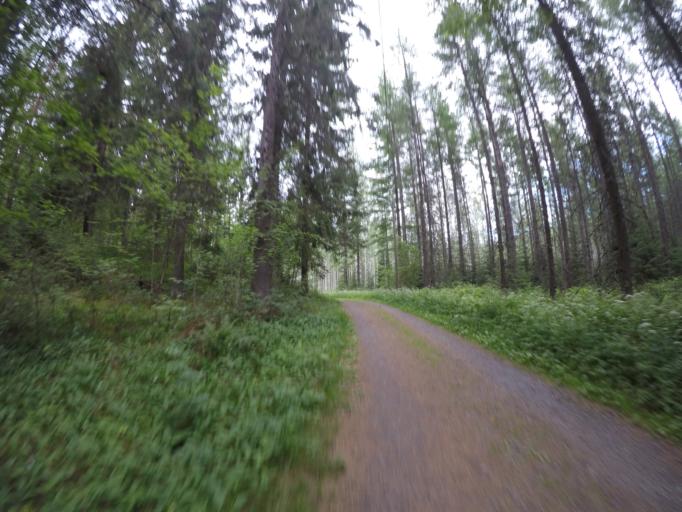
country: FI
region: Haeme
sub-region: Haemeenlinna
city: Haemeenlinna
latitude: 61.0015
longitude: 24.4026
